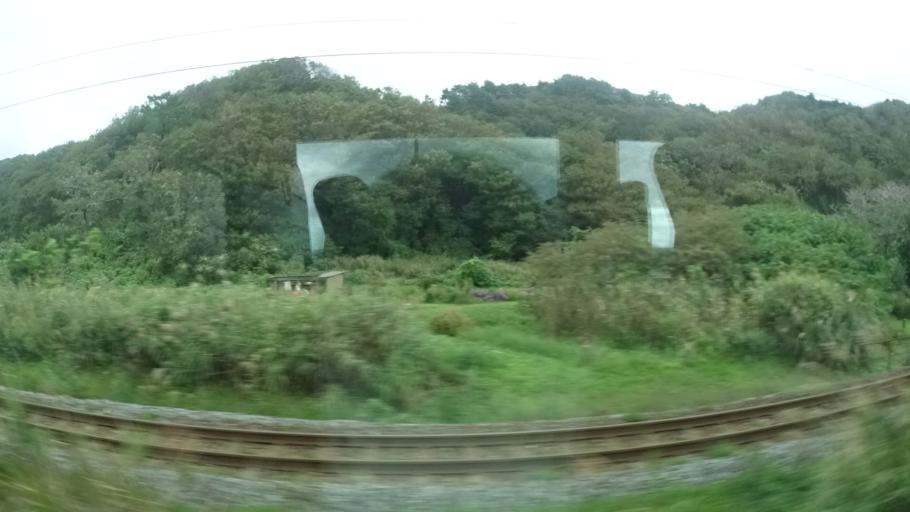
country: JP
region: Niigata
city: Murakami
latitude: 38.3184
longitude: 139.4500
